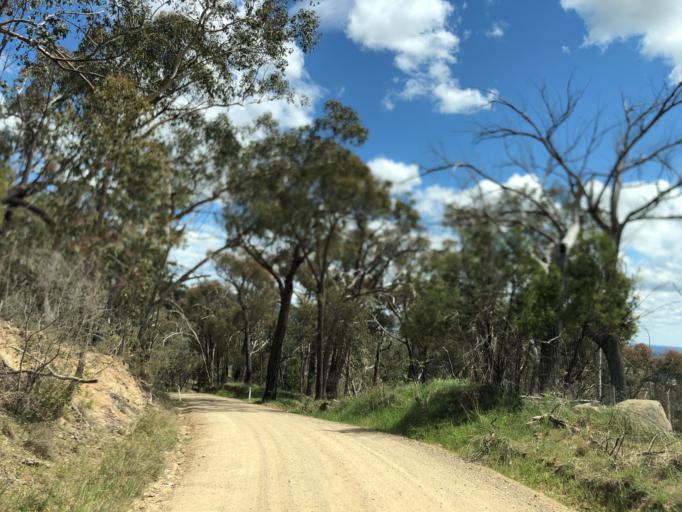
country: AU
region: Victoria
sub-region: Benalla
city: Benalla
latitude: -36.7327
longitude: 146.1374
